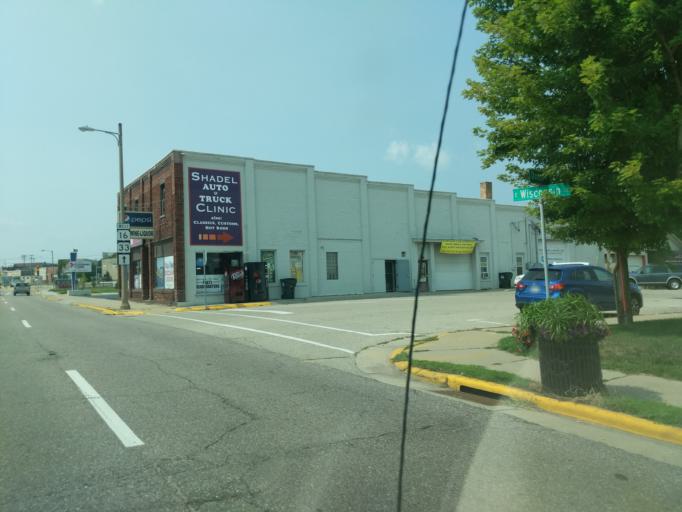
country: US
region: Wisconsin
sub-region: Columbia County
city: Portage
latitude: 43.5380
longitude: -89.4567
